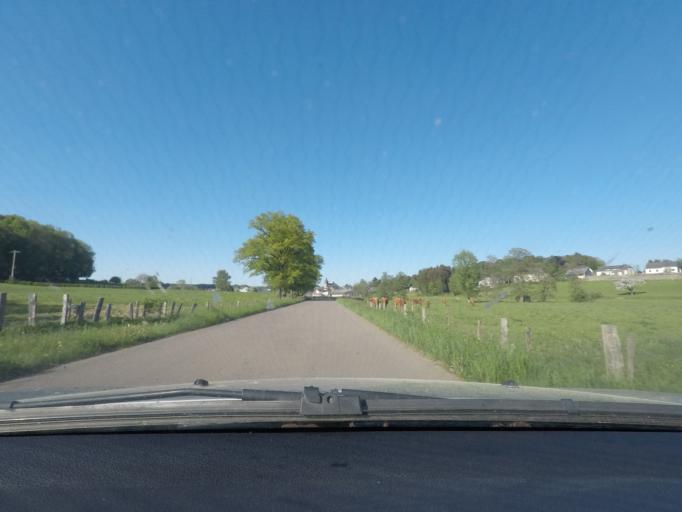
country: BE
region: Wallonia
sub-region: Province du Luxembourg
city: Tintigny
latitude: 49.7133
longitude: 5.4799
